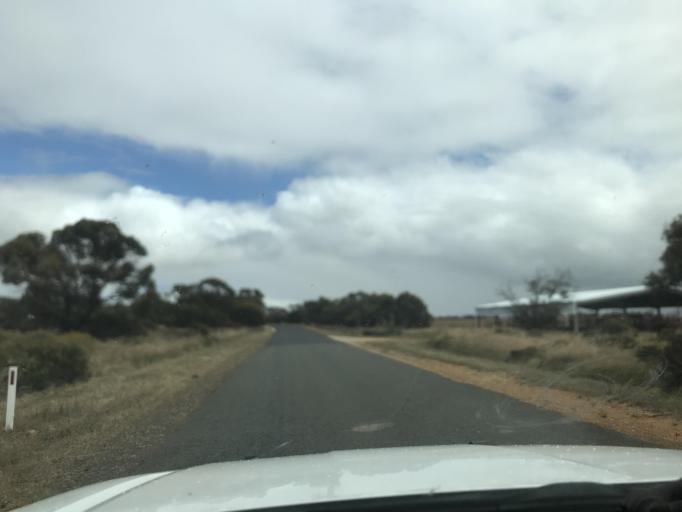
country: AU
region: South Australia
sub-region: Tatiara
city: Bordertown
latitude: -36.1410
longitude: 141.2239
